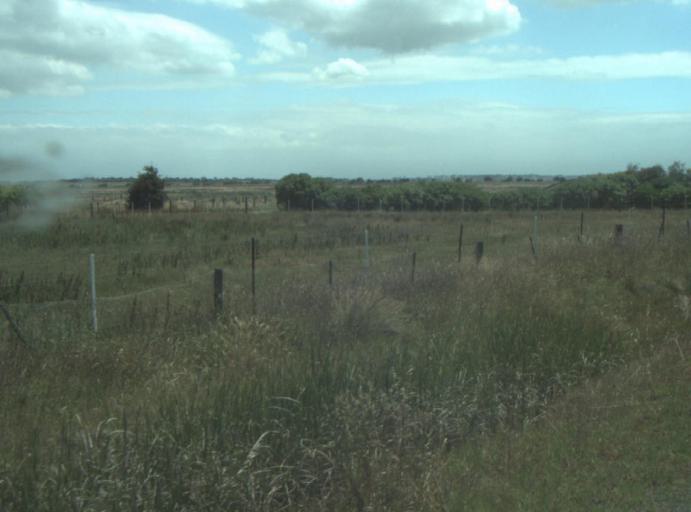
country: AU
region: Victoria
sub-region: Greater Geelong
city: Leopold
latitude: -38.2716
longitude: 144.4375
